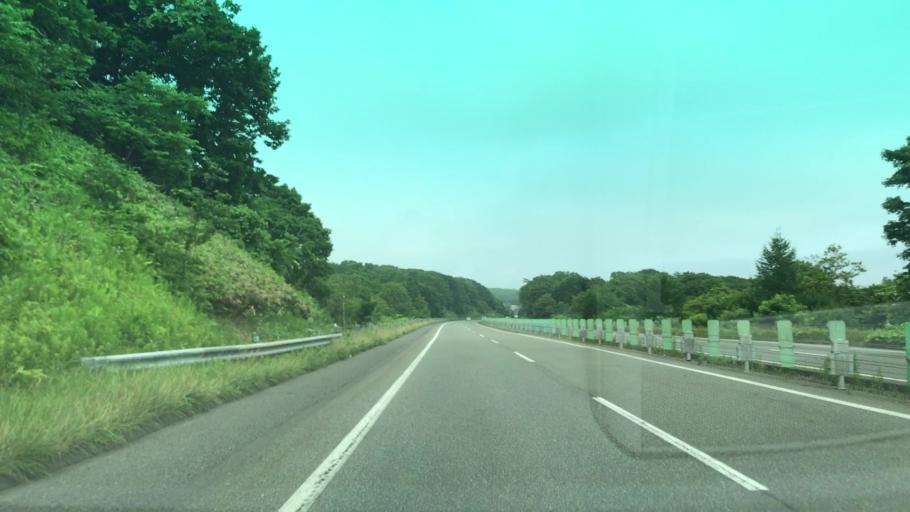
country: JP
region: Hokkaido
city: Shiraoi
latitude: 42.4901
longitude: 141.2368
